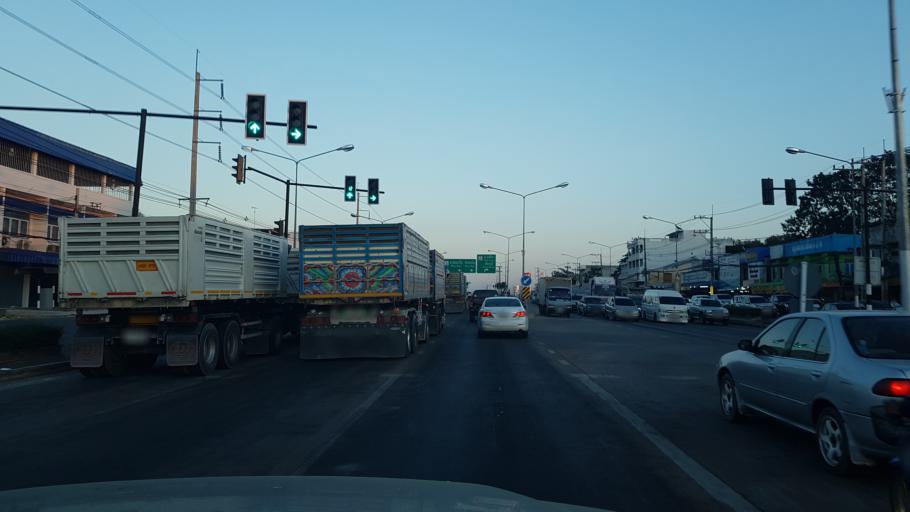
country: TH
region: Khon Kaen
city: Chum Phae
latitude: 16.5425
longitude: 102.1054
